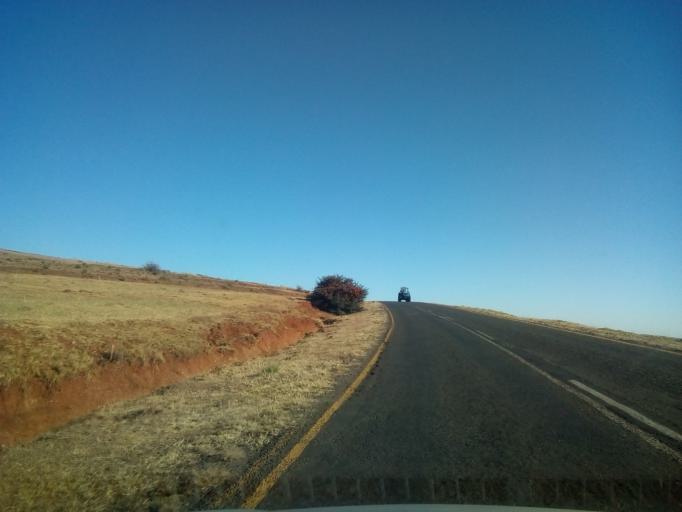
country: LS
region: Berea
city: Teyateyaneng
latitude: -29.2535
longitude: 27.7726
